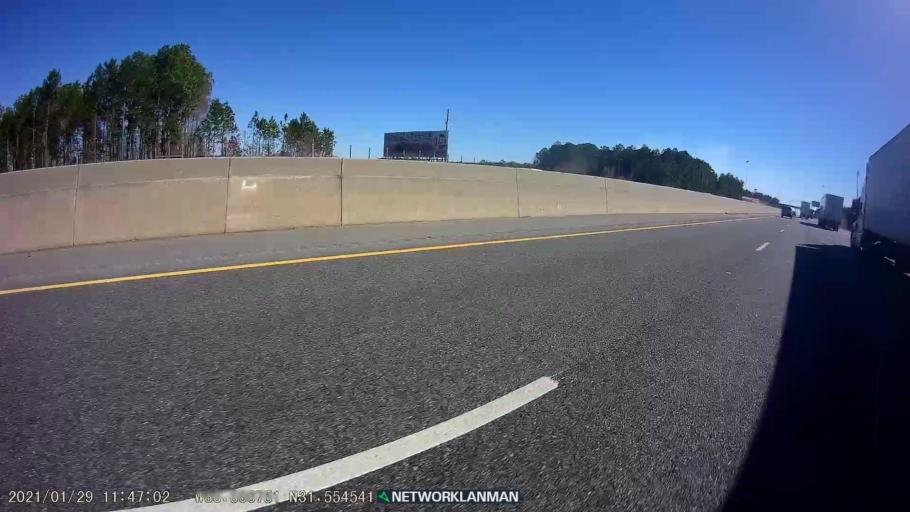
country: US
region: Georgia
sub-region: Tift County
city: Tifton
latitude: 31.5540
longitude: -83.5360
